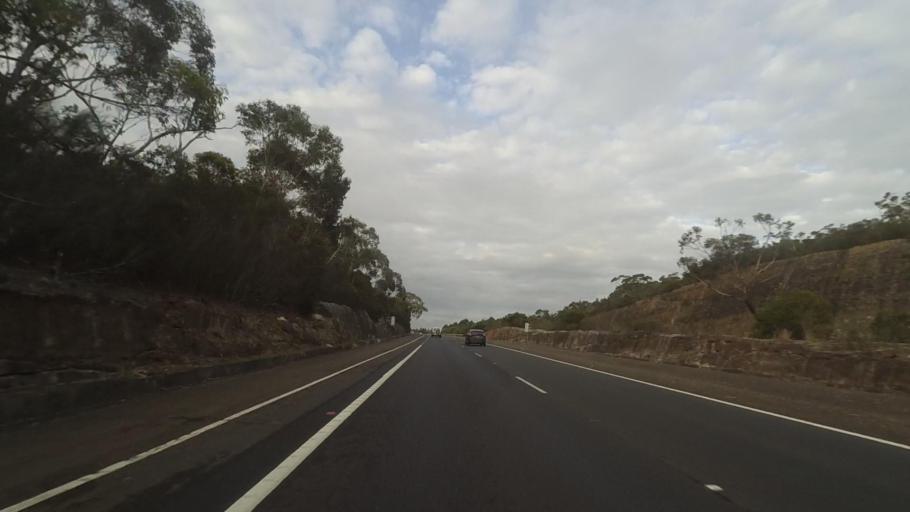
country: AU
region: New South Wales
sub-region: Wollongong
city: Helensburgh
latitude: -34.1532
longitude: 150.9883
